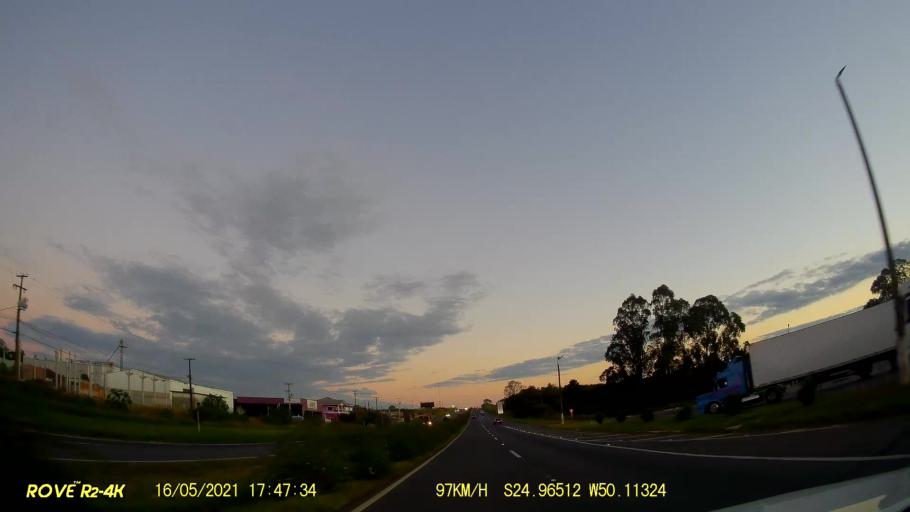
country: BR
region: Parana
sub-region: Carambei
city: Carambei
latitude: -24.9652
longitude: -50.1132
